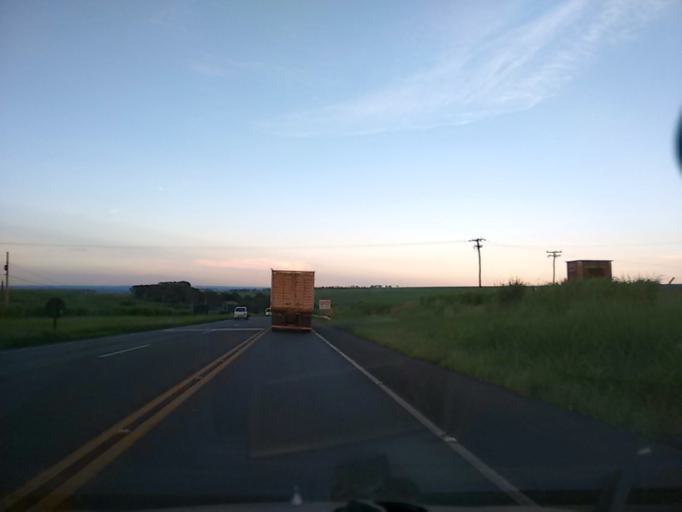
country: BR
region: Sao Paulo
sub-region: Jau
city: Jau
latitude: -22.1515
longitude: -48.4704
